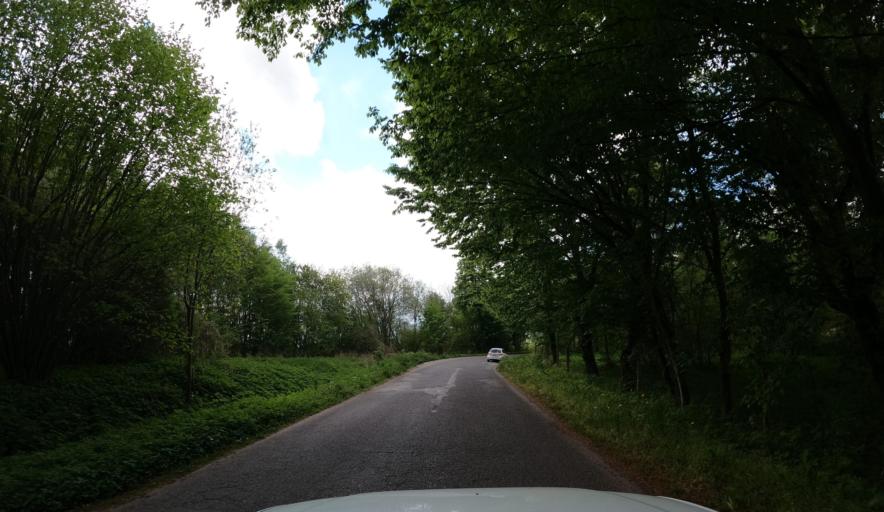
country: PL
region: West Pomeranian Voivodeship
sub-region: Powiat kamienski
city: Wolin
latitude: 53.8495
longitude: 14.6307
